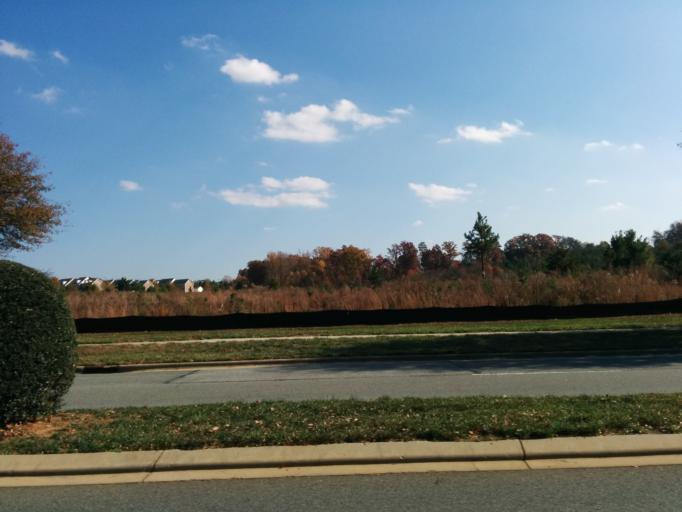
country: US
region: North Carolina
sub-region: Iredell County
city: Mooresville
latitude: 35.5865
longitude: -80.8826
